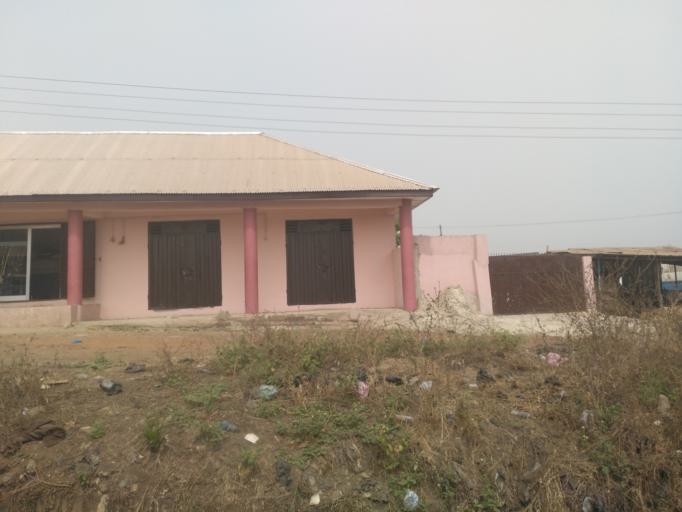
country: GH
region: Ashanti
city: Kumasi
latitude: 6.7019
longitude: -1.5939
